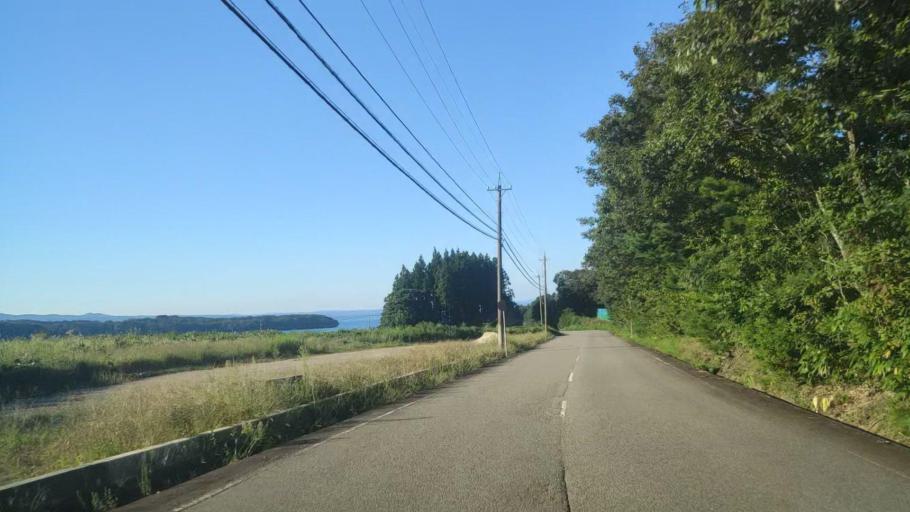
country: JP
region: Ishikawa
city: Nanao
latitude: 37.1303
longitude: 136.9311
